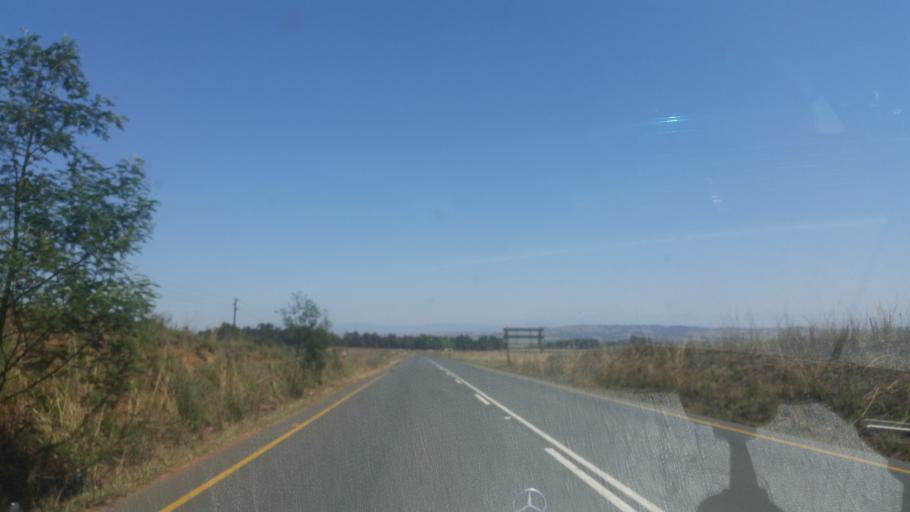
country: ZA
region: KwaZulu-Natal
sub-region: uMgungundlovu District Municipality
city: Mooirivier
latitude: -29.1439
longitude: 29.9928
